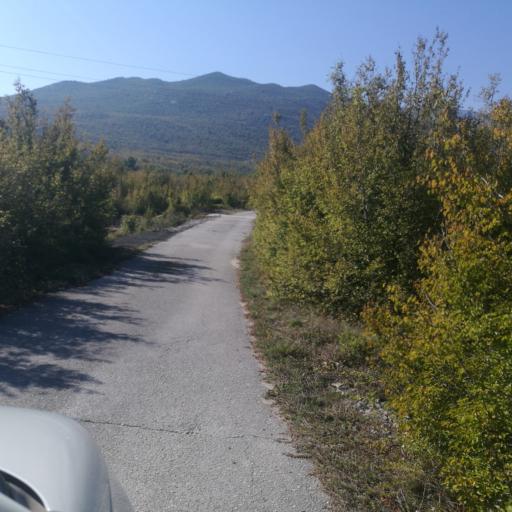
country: HR
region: Splitsko-Dalmatinska
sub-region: Grad Omis
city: Omis
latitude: 43.5180
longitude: 16.7580
